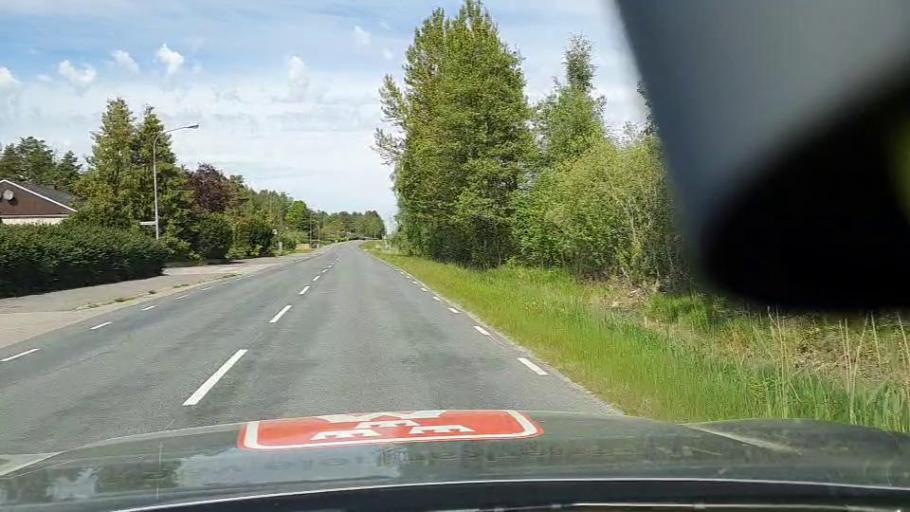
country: SE
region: Soedermanland
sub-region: Eskilstuna Kommun
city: Skogstorp
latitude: 59.2960
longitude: 16.4582
